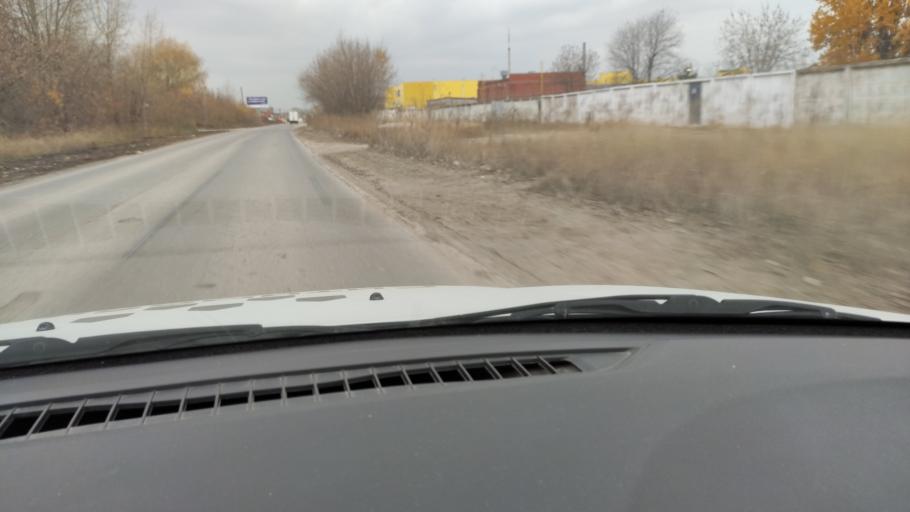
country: RU
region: Perm
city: Froly
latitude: 57.9563
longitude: 56.2716
